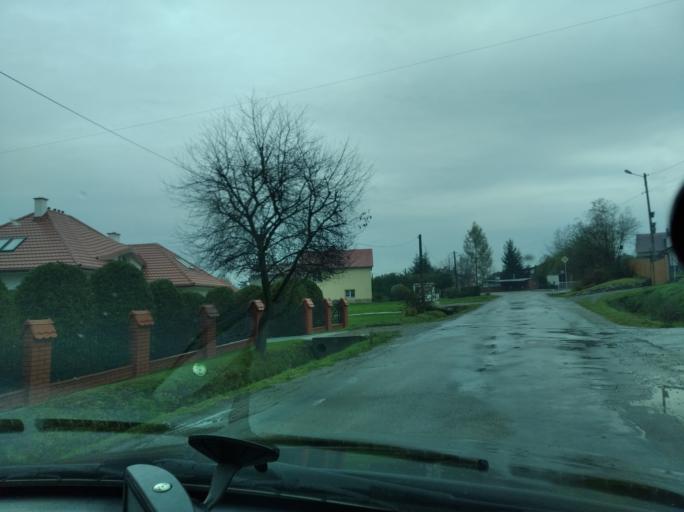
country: PL
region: Subcarpathian Voivodeship
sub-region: Powiat strzyzowski
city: Czudec
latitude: 49.9308
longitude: 21.8480
